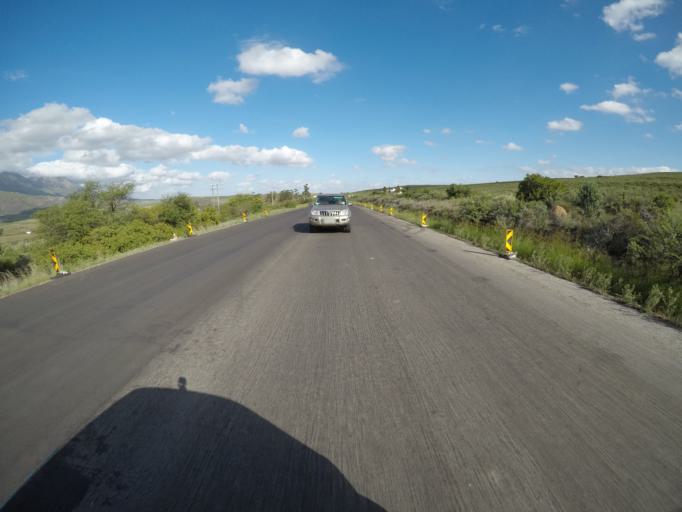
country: ZA
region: Western Cape
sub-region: Cape Winelands District Municipality
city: Ashton
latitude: -33.9361
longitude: 20.2122
